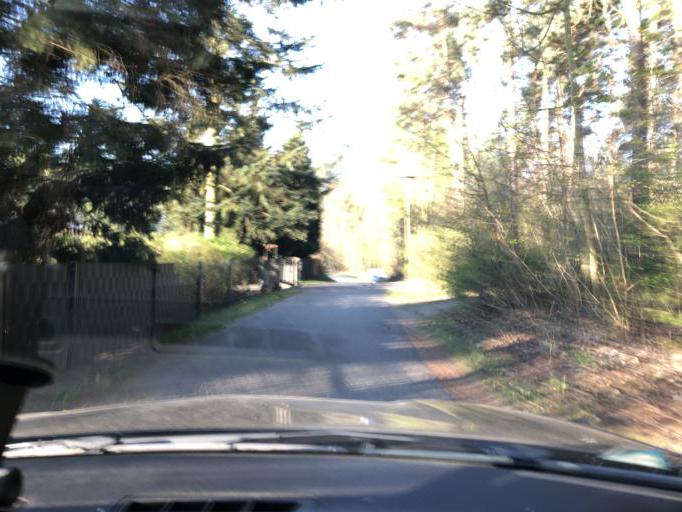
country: DE
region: Saxony
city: Krauschwitz
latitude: 51.5145
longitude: 14.7100
